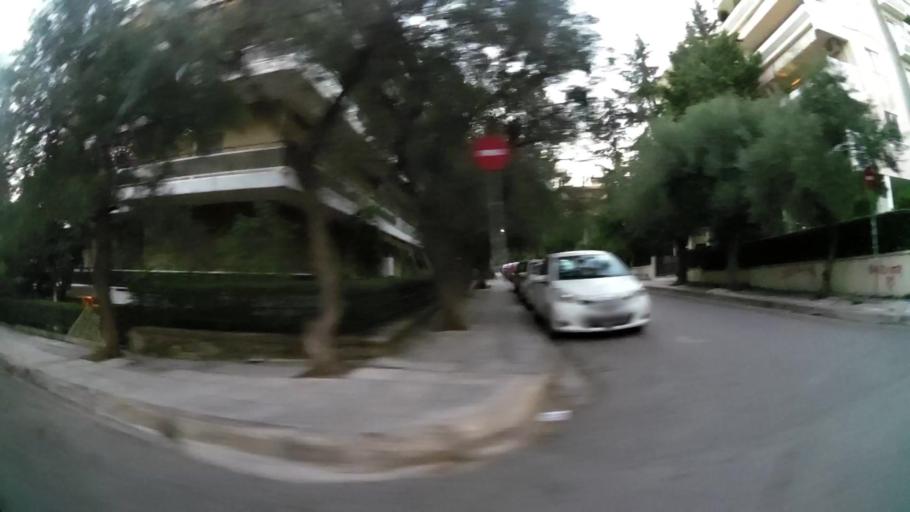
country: GR
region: Attica
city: Pefki
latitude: 38.0605
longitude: 23.8017
